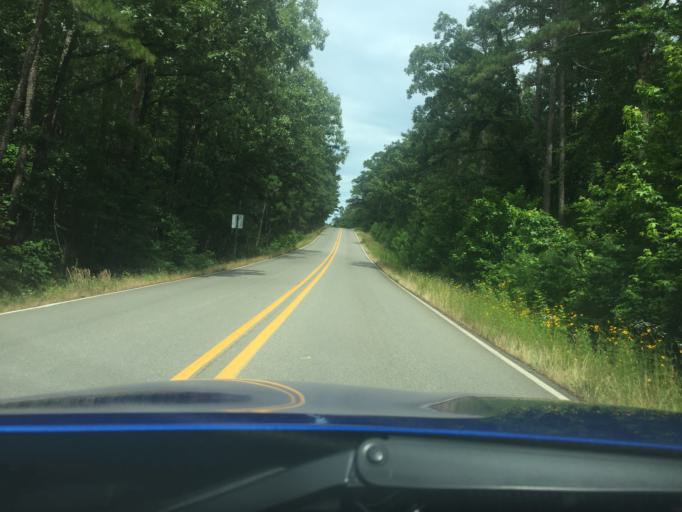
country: US
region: Arkansas
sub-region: Pulaski County
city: Maumelle
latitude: 34.8351
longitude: -92.4634
